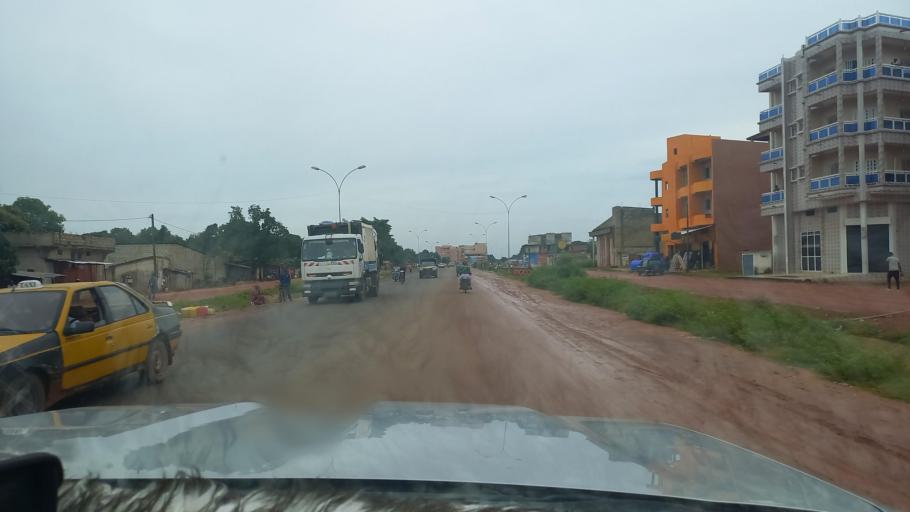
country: SN
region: Ziguinchor
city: Ziguinchor
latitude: 12.5547
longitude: -16.2665
